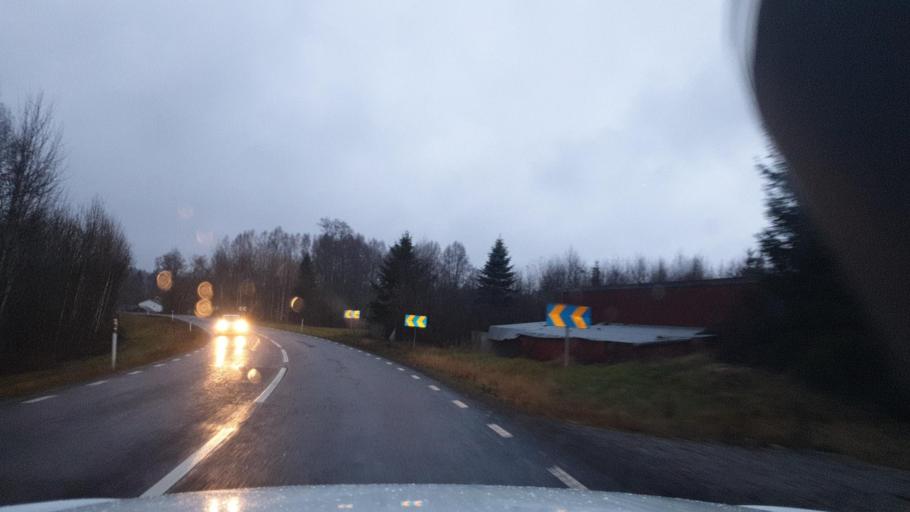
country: SE
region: Vaermland
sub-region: Eda Kommun
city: Charlottenberg
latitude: 59.8295
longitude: 12.3152
